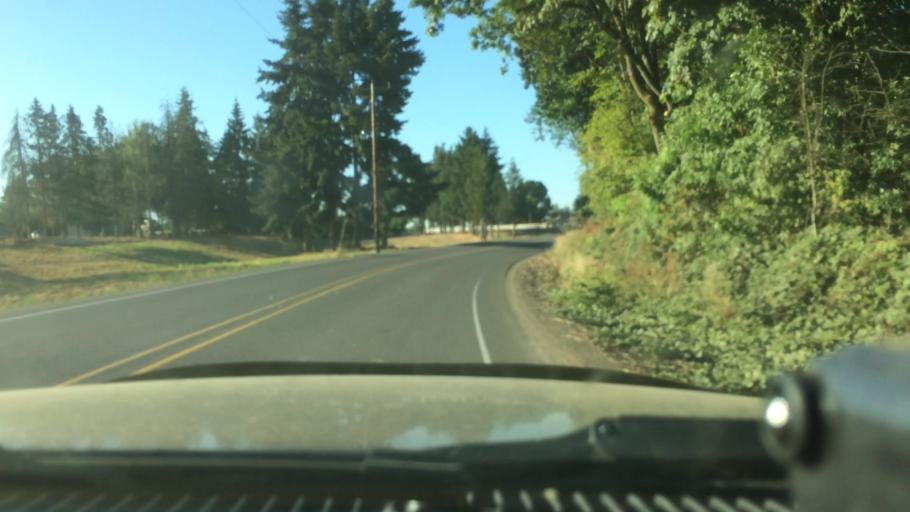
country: US
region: Oregon
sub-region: Marion County
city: Gervais
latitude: 45.1192
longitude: -122.9832
